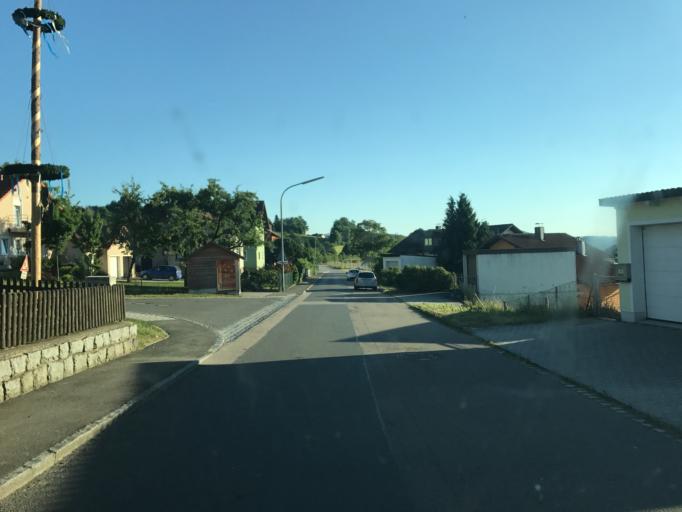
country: DE
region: Bavaria
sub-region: Upper Palatinate
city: Waldmunchen
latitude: 49.3887
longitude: 12.7146
